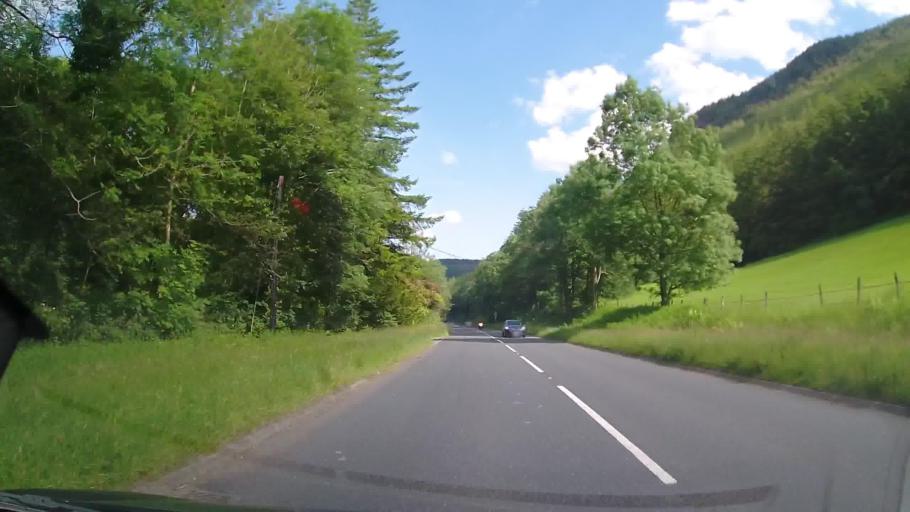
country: GB
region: Wales
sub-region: Gwynedd
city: Corris
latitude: 52.7239
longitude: -3.7056
